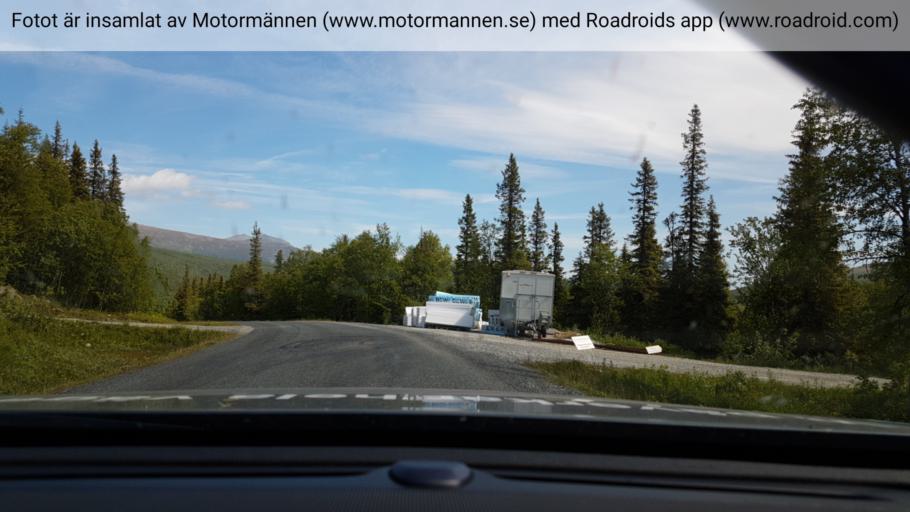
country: SE
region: Vaesterbotten
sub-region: Vilhelmina Kommun
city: Sjoberg
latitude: 65.2382
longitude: 15.4688
